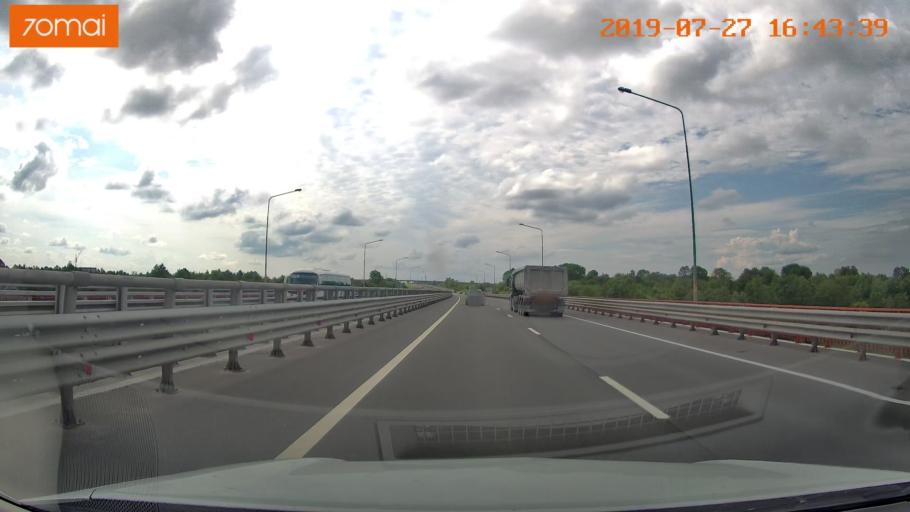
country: RU
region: Kaliningrad
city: Gvardeysk
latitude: 54.6718
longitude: 21.0980
